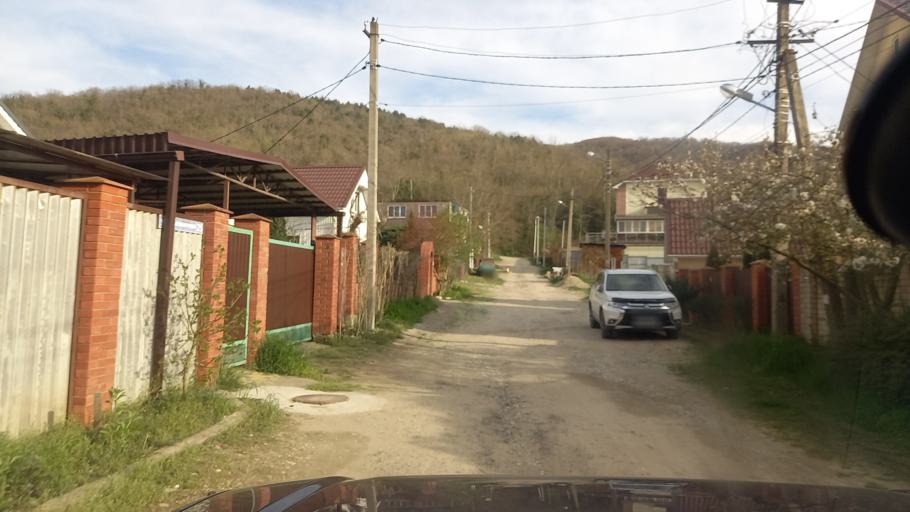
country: RU
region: Krasnodarskiy
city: Arkhipo-Osipovka
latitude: 44.3670
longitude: 38.5469
